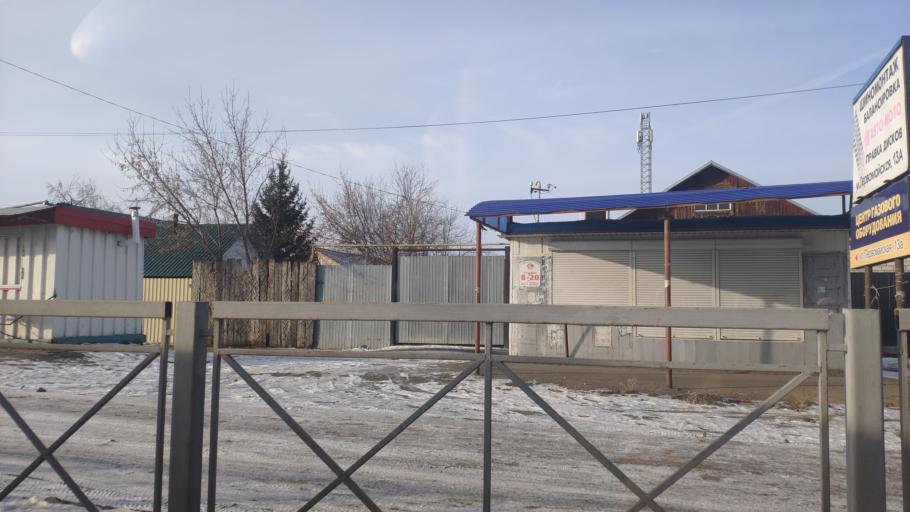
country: RU
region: Kurgan
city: Shadrinsk
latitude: 56.0881
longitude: 63.6736
